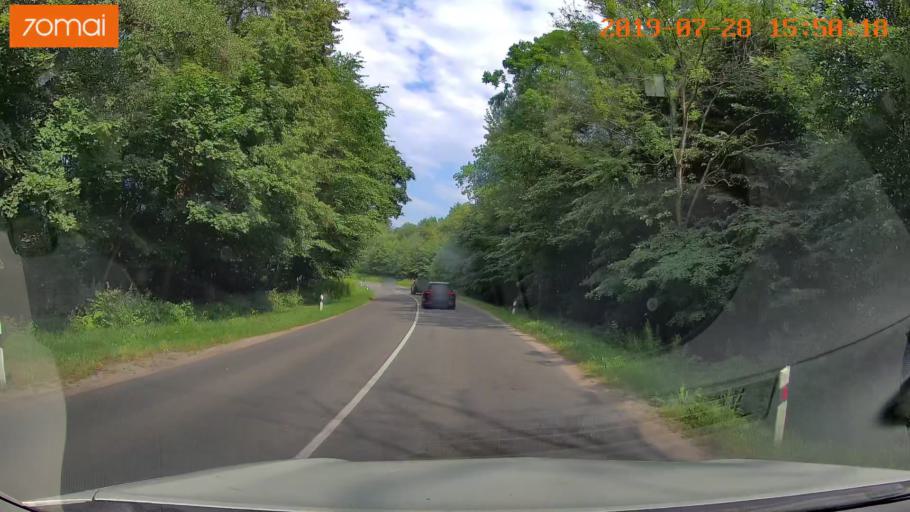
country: RU
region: Kaliningrad
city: Otradnoye
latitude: 54.9397
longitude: 20.0898
